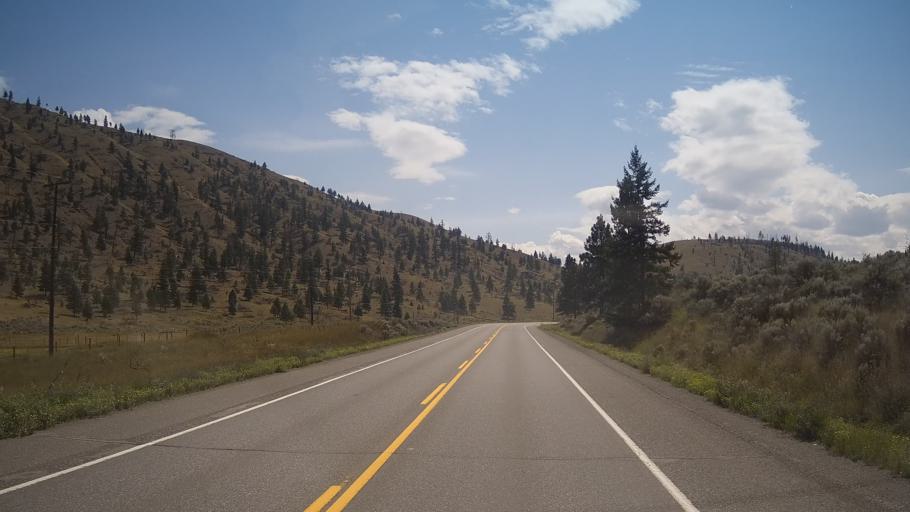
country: CA
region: British Columbia
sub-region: Thompson-Nicola Regional District
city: Ashcroft
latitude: 50.6461
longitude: -121.3485
